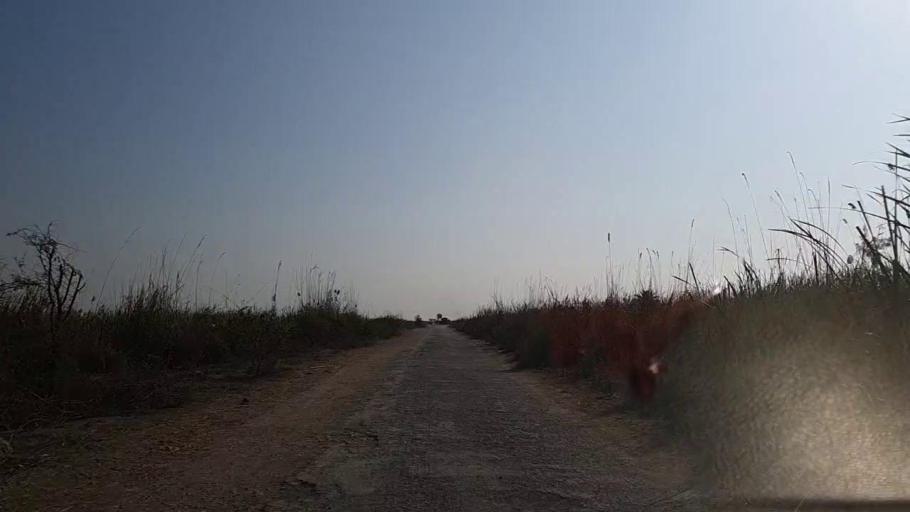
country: PK
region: Sindh
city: Tando Mittha Khan
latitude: 25.8877
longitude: 69.0768
